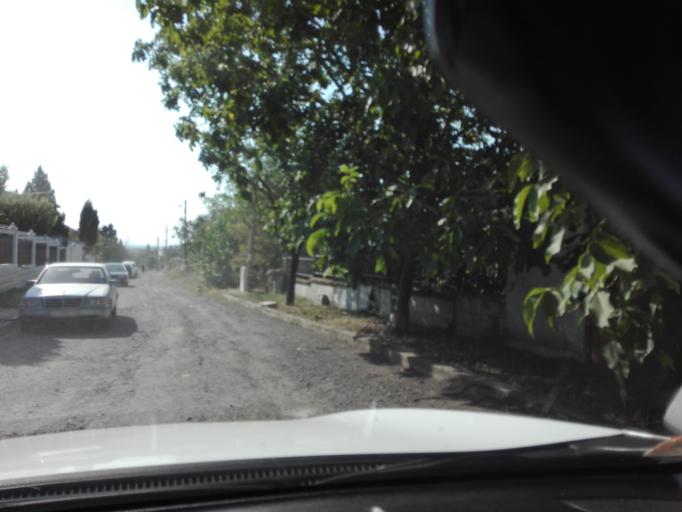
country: BG
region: Burgas
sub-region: Obshtina Kameno
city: Kameno
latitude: 42.6266
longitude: 27.3878
